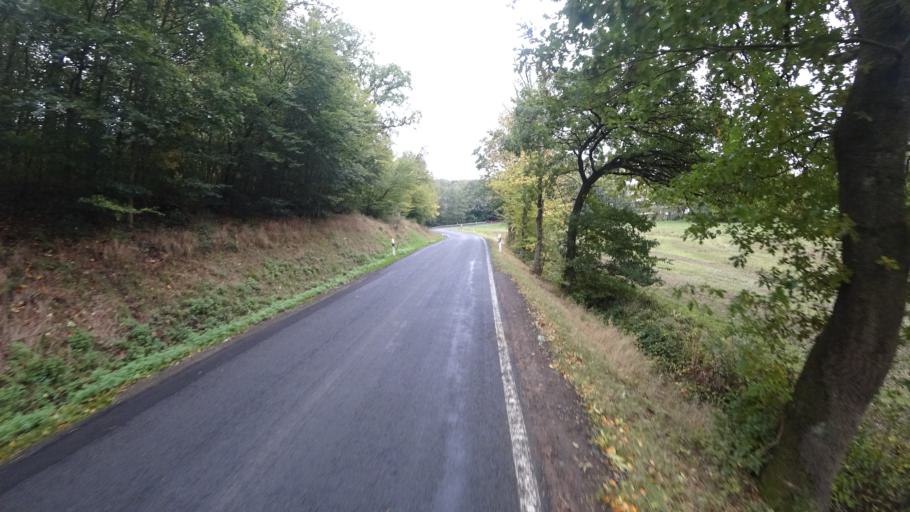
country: DE
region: Rheinland-Pfalz
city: Oberhaid
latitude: 50.5101
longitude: 7.7224
